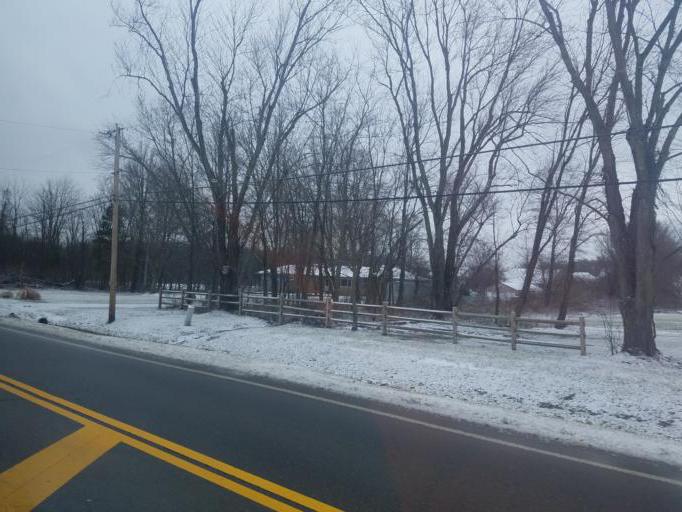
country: US
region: Ohio
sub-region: Franklin County
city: New Albany
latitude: 40.0428
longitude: -82.7923
